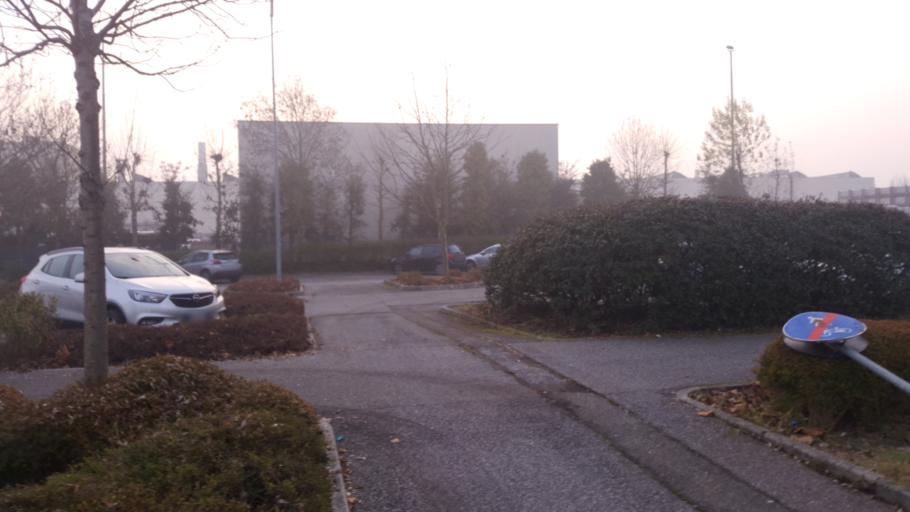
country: IT
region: Emilia-Romagna
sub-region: Provincia di Ravenna
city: Faenza
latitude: 44.3034
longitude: 11.8985
